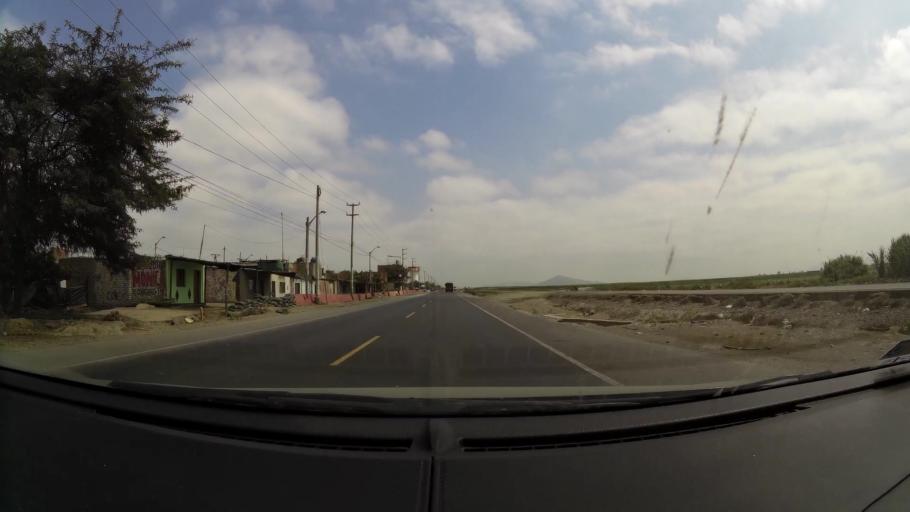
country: PE
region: La Libertad
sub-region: Ascope
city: Chicama
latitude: -7.8353
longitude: -79.1568
